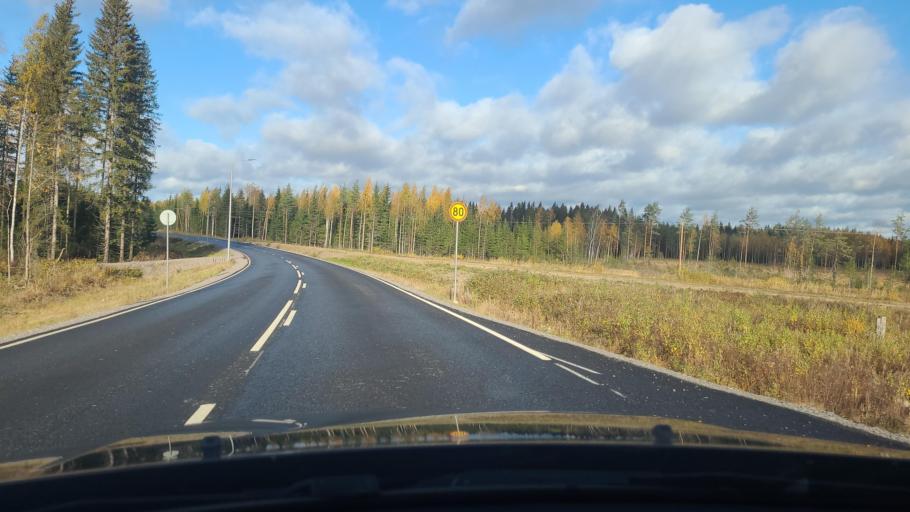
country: FI
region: Southern Savonia
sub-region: Pieksaemaeki
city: Juva
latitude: 61.8790
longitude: 27.7649
